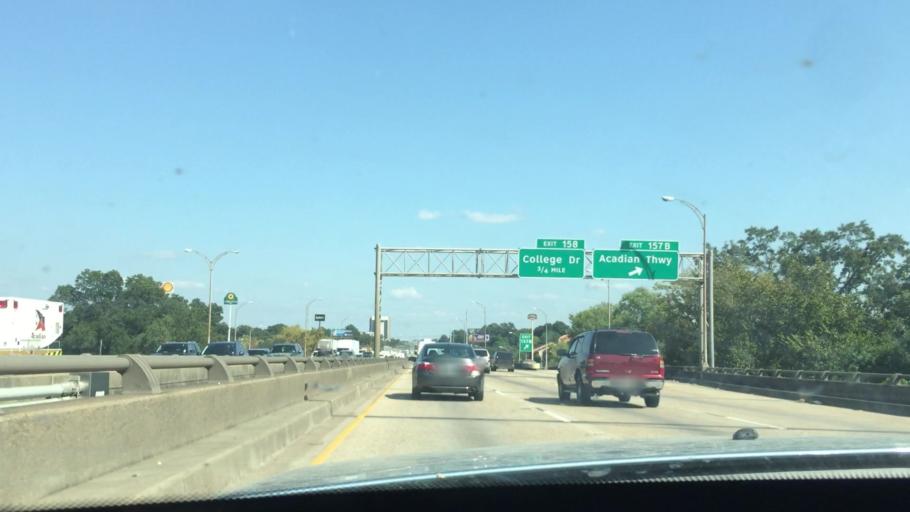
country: US
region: Louisiana
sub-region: East Baton Rouge Parish
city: Baton Rouge
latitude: 30.4245
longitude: -91.1546
